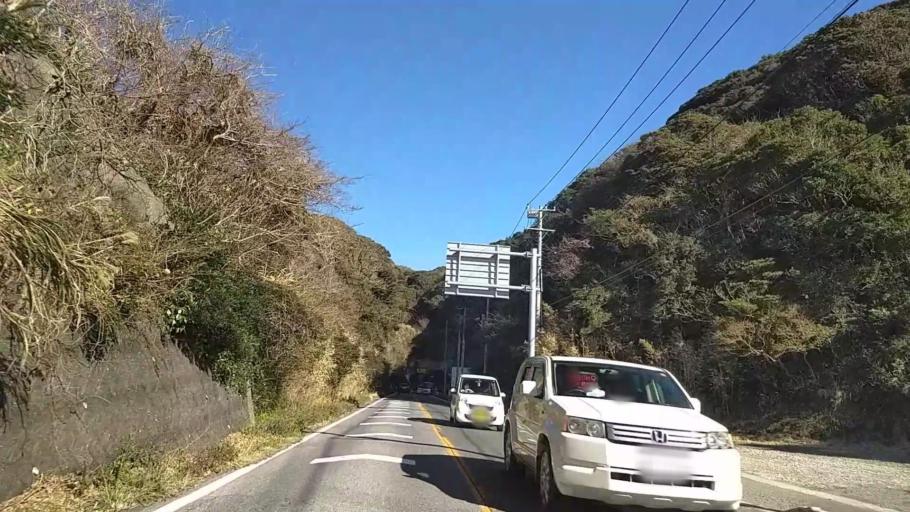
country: JP
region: Chiba
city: Katsuura
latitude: 35.1402
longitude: 140.2752
